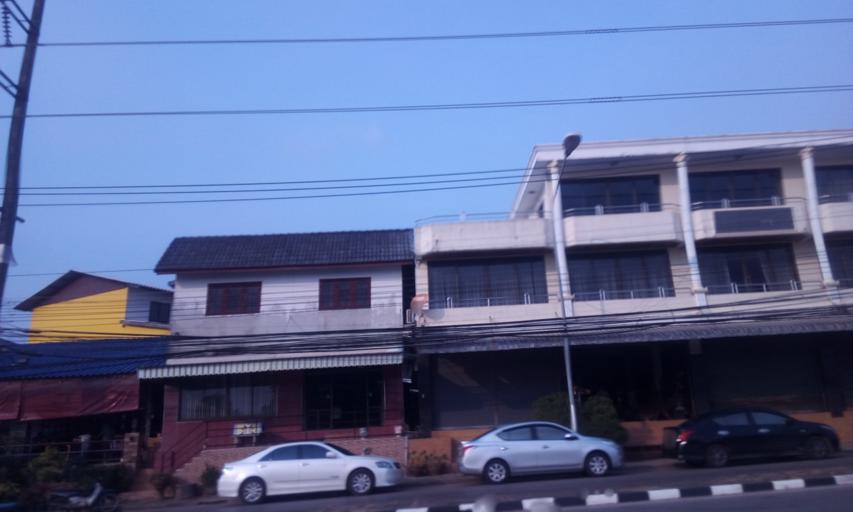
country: TH
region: Trat
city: Khao Saming
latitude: 12.3766
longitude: 102.3808
